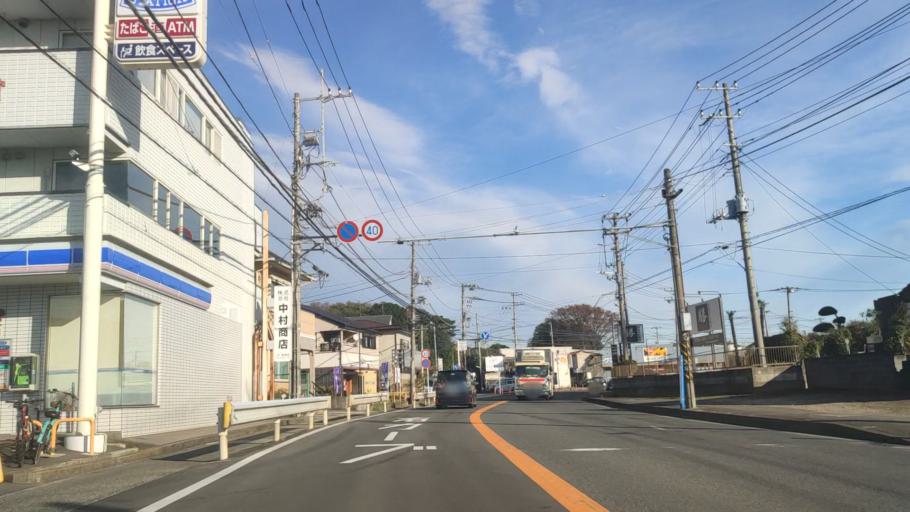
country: JP
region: Kanagawa
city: Atsugi
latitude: 35.4217
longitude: 139.3950
